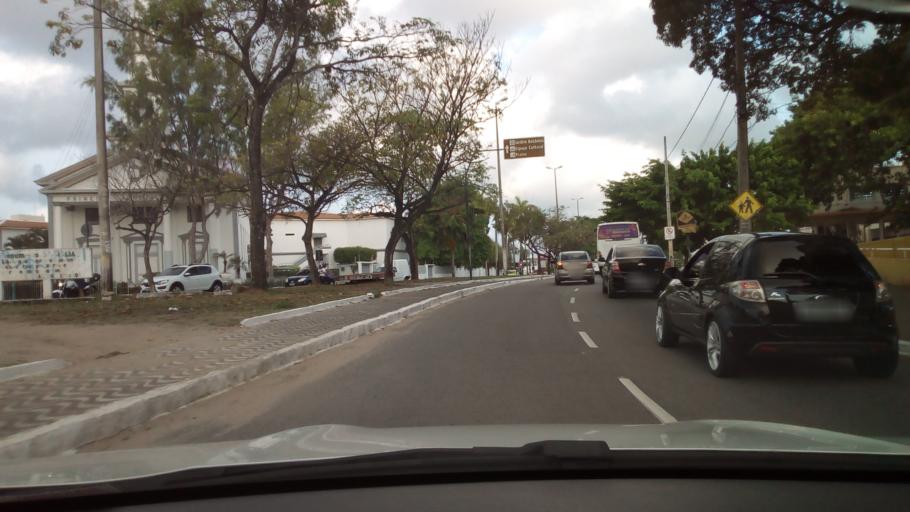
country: BR
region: Paraiba
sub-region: Joao Pessoa
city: Joao Pessoa
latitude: -7.1211
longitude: -34.8753
